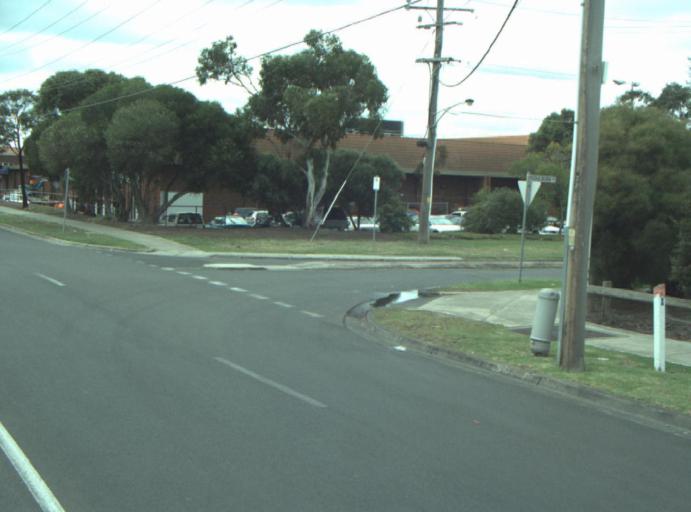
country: AU
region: Victoria
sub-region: Greater Geelong
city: Bell Park
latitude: -38.0736
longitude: 144.3545
